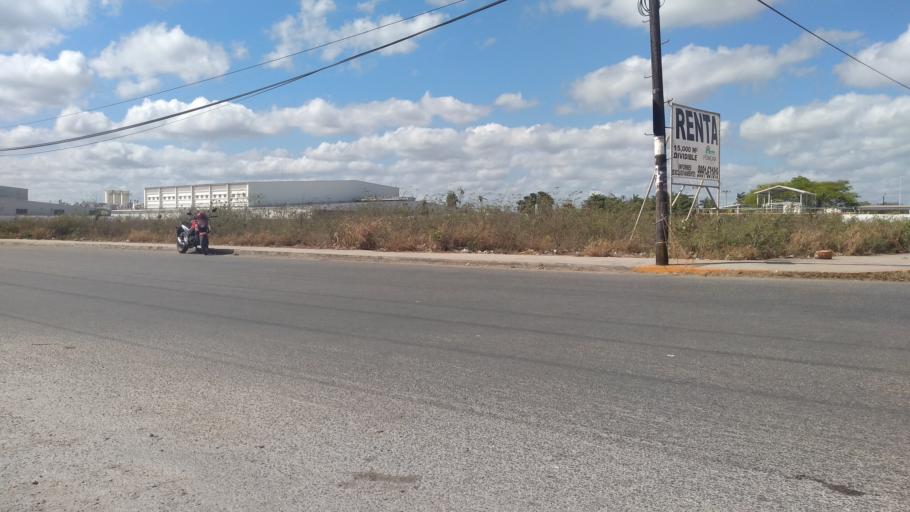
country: MX
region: Yucatan
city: Itzincab Palomeque
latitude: 20.9306
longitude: -89.6765
